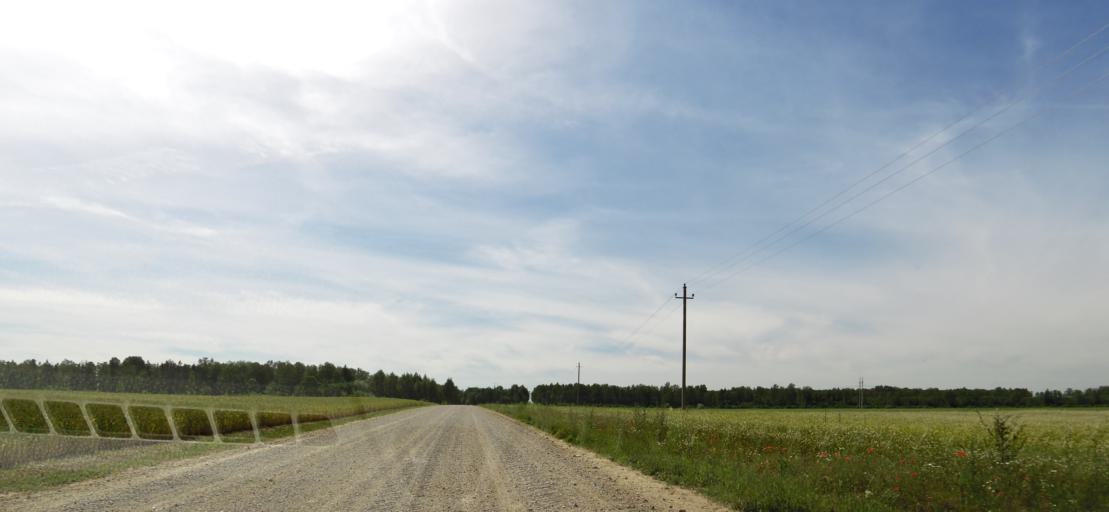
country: LT
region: Panevezys
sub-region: Panevezys City
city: Panevezys
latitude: 55.8830
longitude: 24.3209
